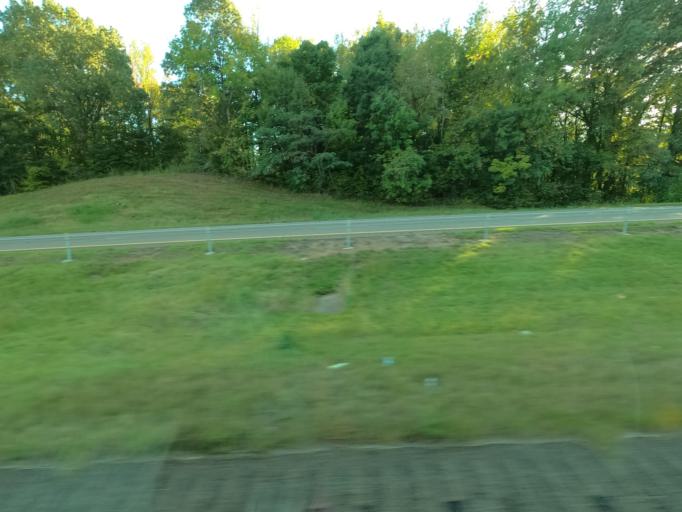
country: US
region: Tennessee
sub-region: Shelby County
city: Arlington
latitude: 35.3090
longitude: -89.7046
